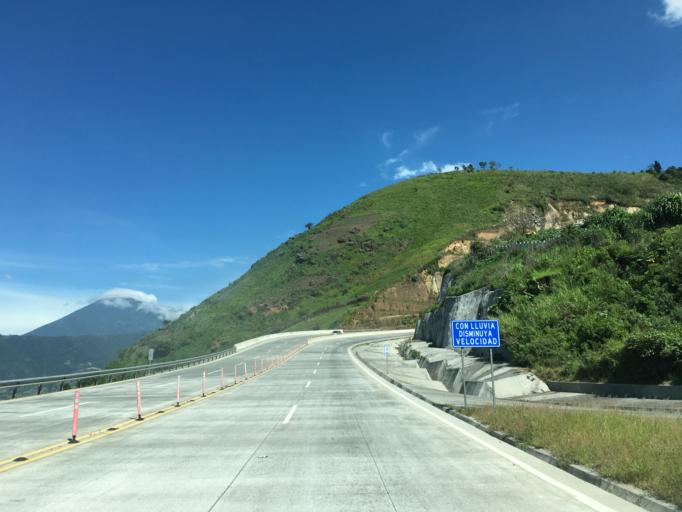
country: GT
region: Guatemala
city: Amatitlan
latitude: 14.4882
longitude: -90.5946
